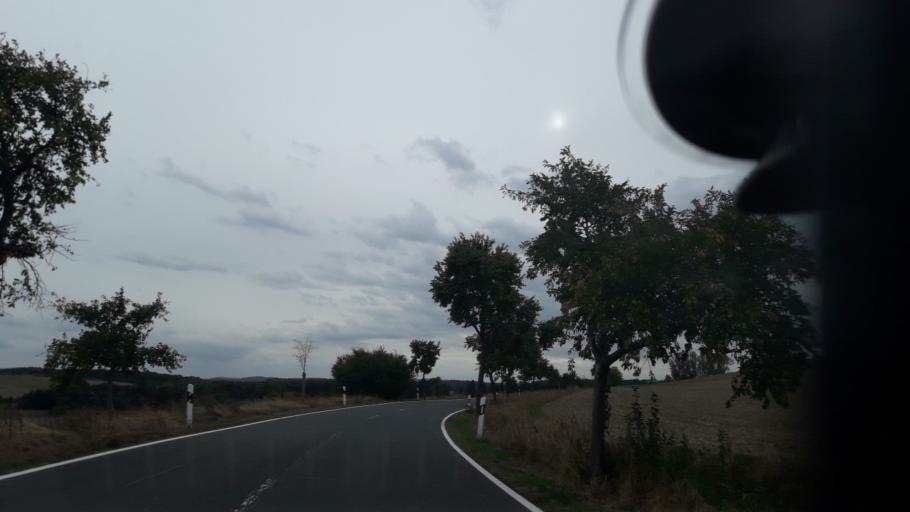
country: DE
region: Lower Saxony
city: Werlaburgdorf
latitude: 52.0505
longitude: 10.5238
